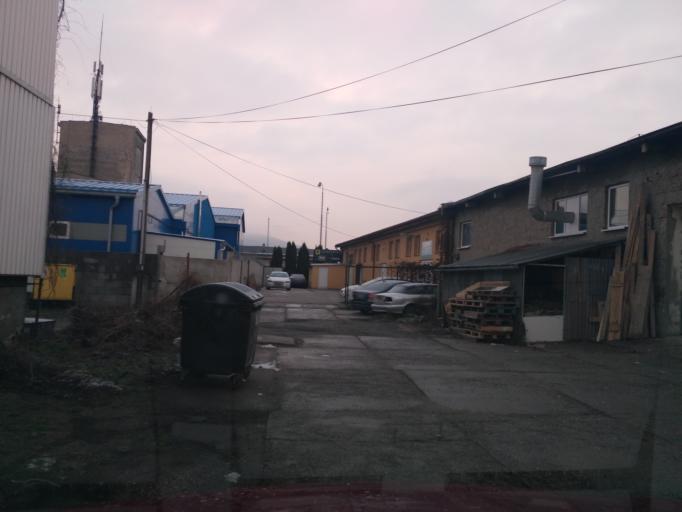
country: SK
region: Kosicky
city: Kosice
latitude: 48.7377
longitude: 21.2652
